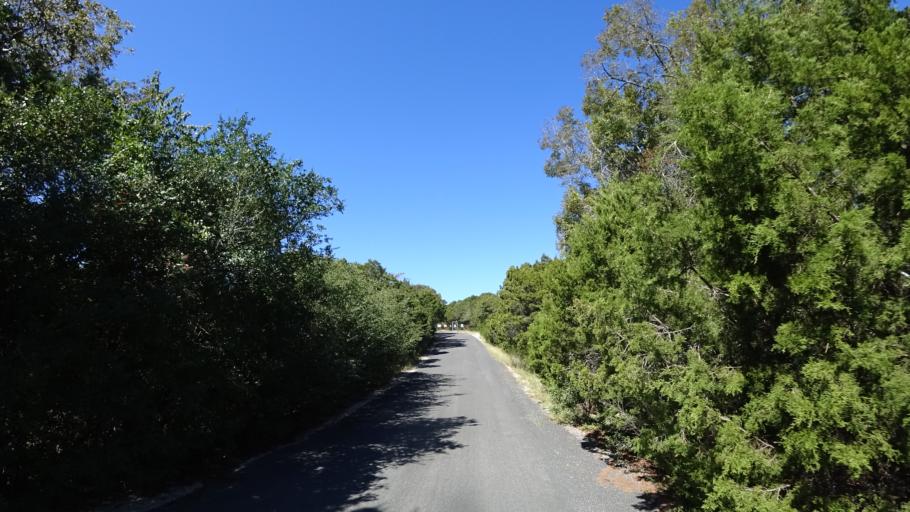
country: US
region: Texas
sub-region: Travis County
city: West Lake Hills
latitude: 30.3067
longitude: -97.8153
